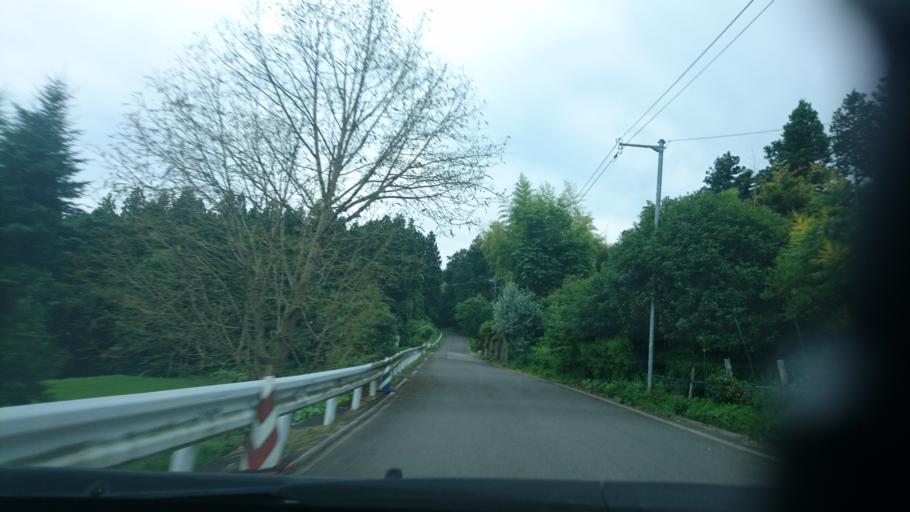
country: JP
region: Iwate
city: Ichinoseki
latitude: 38.8957
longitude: 141.3077
